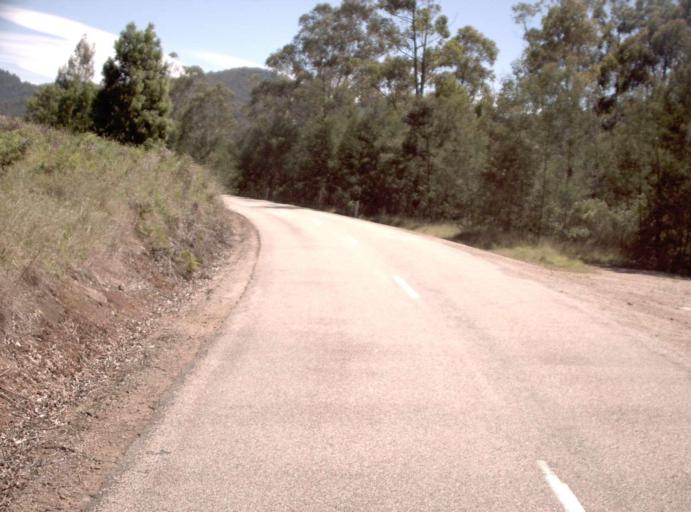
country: AU
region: Victoria
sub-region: East Gippsland
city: Lakes Entrance
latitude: -37.4018
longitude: 148.2142
